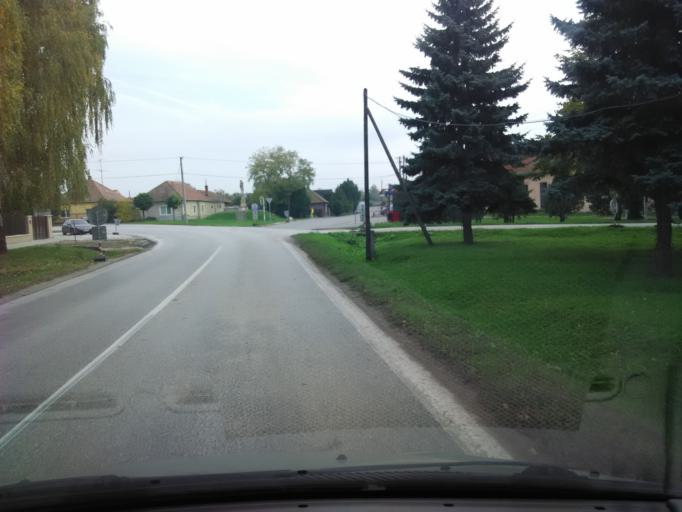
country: SK
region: Nitriansky
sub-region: Okres Nove Zamky
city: Nove Zamky
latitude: 47.9921
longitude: 18.2696
